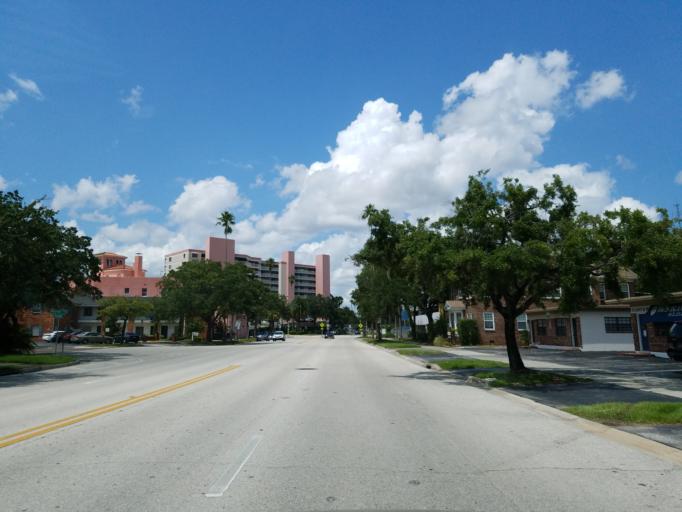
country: US
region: Florida
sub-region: Hillsborough County
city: Tampa
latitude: 27.9350
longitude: -82.4586
